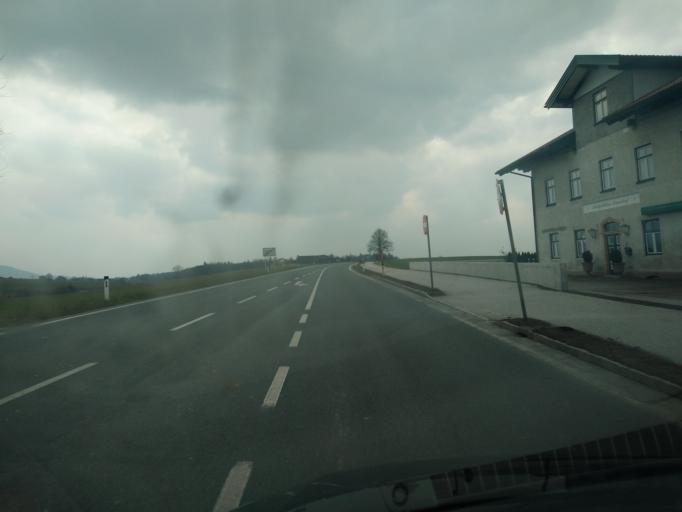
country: AT
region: Salzburg
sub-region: Politischer Bezirk Salzburg-Umgebung
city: Lamprechtshausen
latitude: 47.9662
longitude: 12.9485
